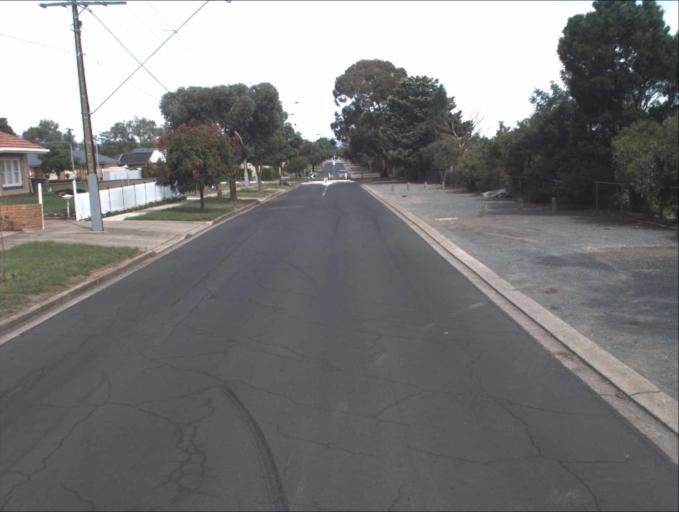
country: AU
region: South Australia
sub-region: Port Adelaide Enfield
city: Enfield
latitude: -34.8562
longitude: 138.6143
